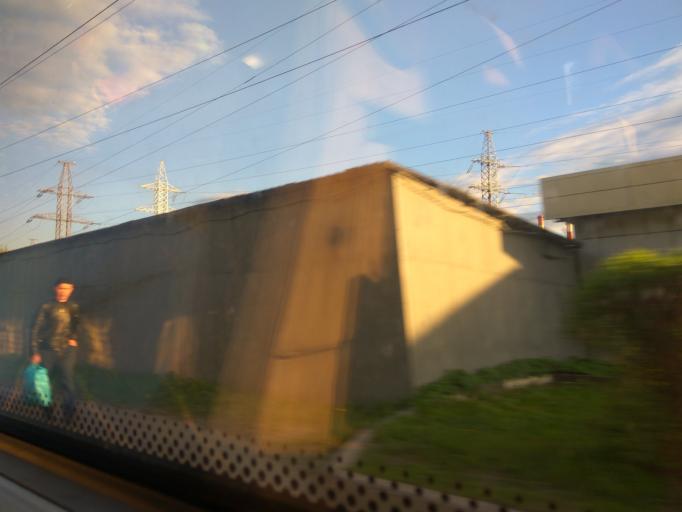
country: RU
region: Moscow
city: Tsaritsyno
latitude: 55.6508
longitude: 37.6439
